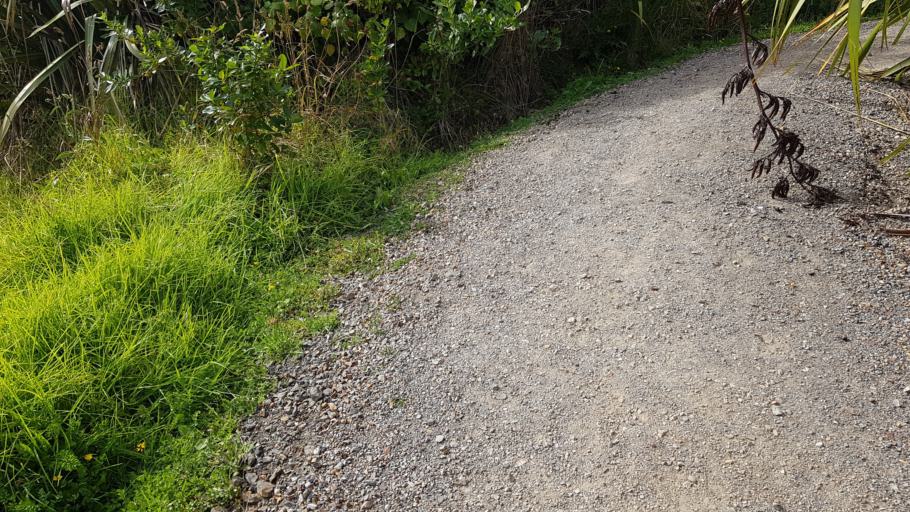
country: NZ
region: Auckland
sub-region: Auckland
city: Rothesay Bay
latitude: -36.6674
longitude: 174.7457
